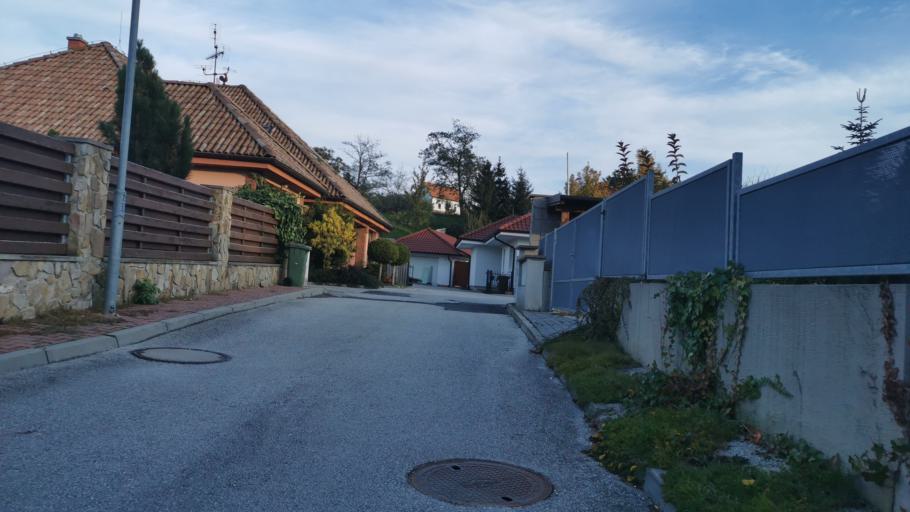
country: SK
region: Trnavsky
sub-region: Okres Skalica
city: Skalica
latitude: 48.8341
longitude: 17.2301
